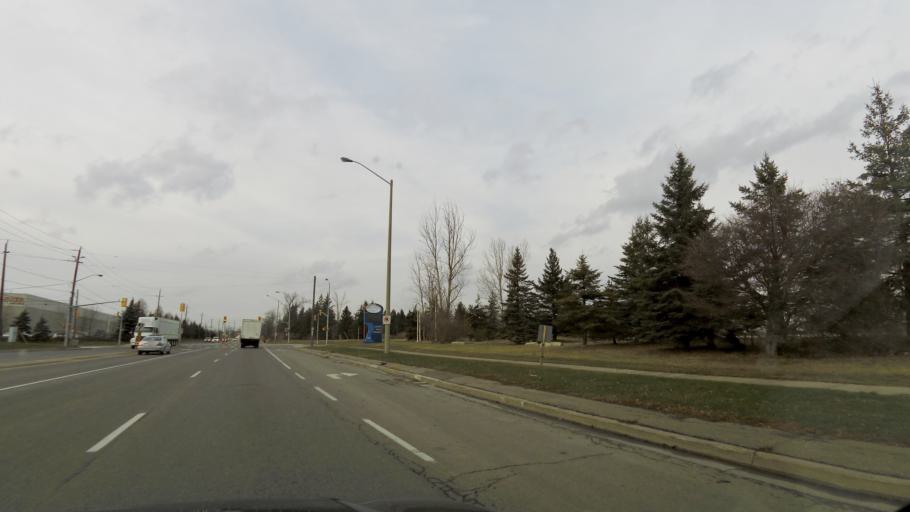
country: CA
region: Ontario
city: Etobicoke
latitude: 43.7394
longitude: -79.6426
